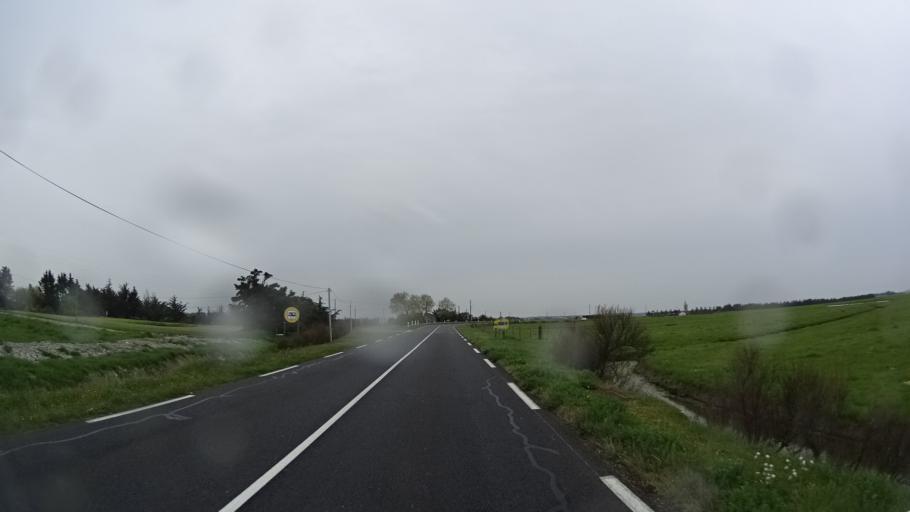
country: FR
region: Pays de la Loire
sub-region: Departement de la Vendee
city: Beauvoir-sur-Mer
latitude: 46.8886
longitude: -2.0730
